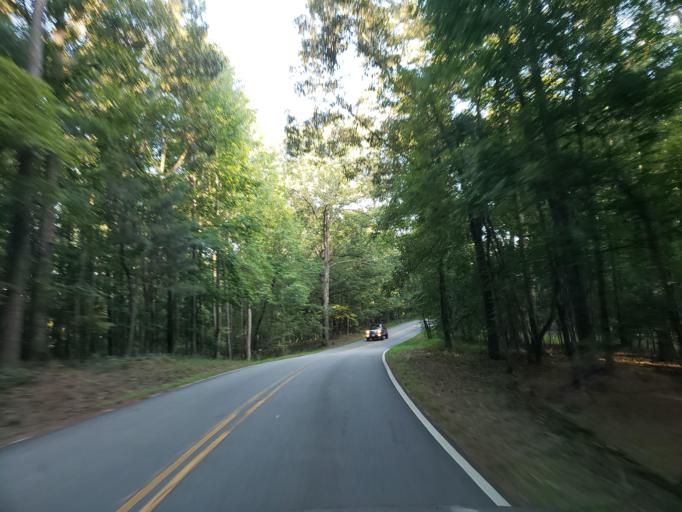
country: US
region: Georgia
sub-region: Bartow County
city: Emerson
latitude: 34.1829
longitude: -84.7068
